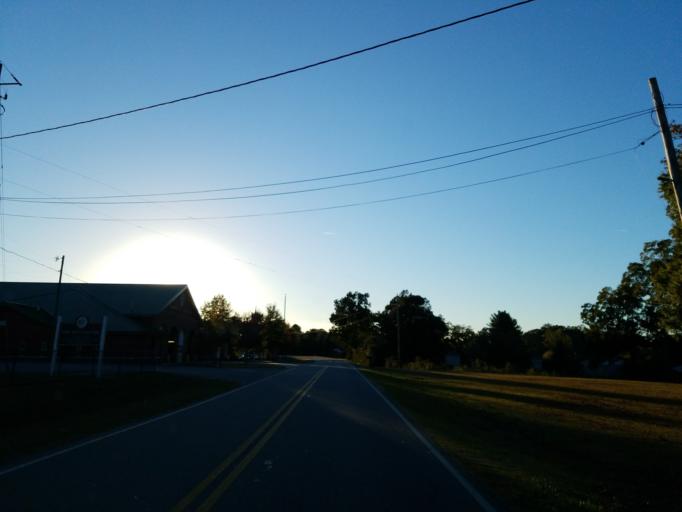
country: US
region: Georgia
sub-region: Forsyth County
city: Cumming
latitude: 34.2723
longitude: -84.0920
